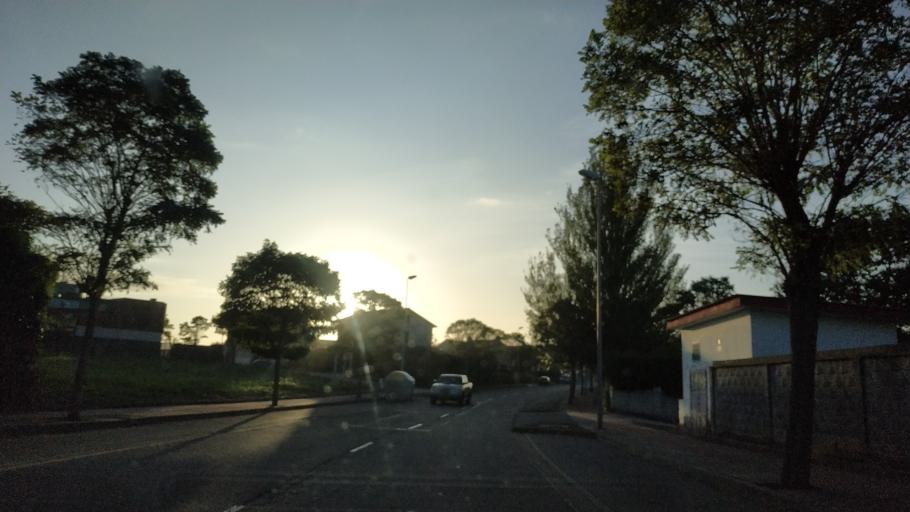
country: ES
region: Galicia
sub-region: Provincia da Coruna
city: Oleiros
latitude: 43.3701
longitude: -8.3379
